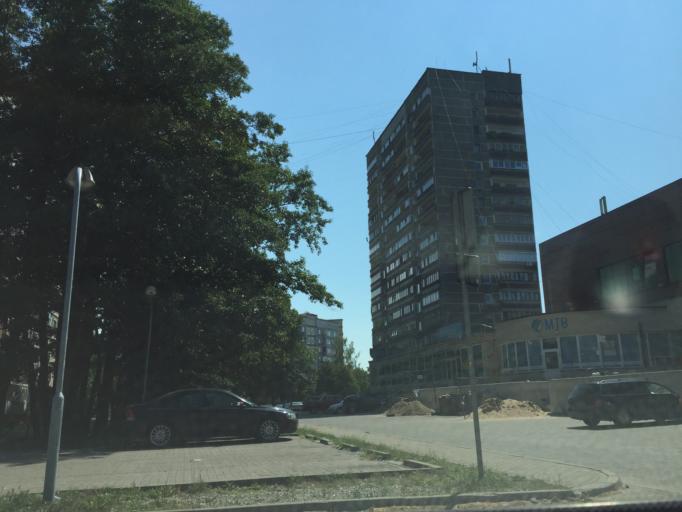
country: LV
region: Marupe
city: Marupe
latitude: 56.9493
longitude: 24.0003
